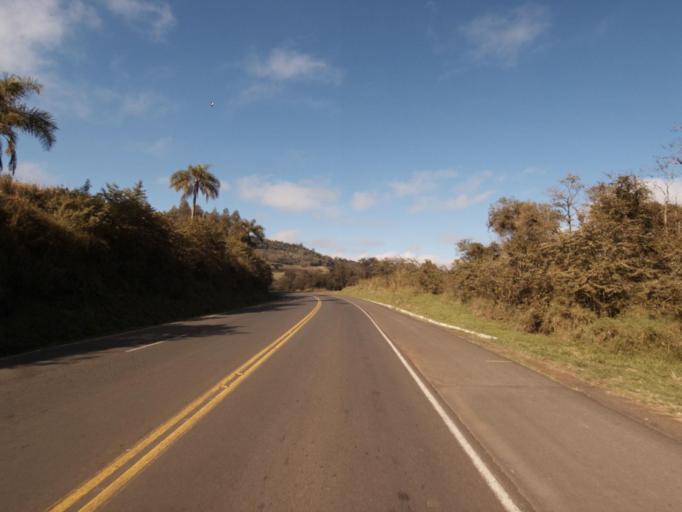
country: BR
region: Rio Grande do Sul
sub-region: Frederico Westphalen
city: Frederico Westphalen
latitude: -27.0749
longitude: -53.2315
